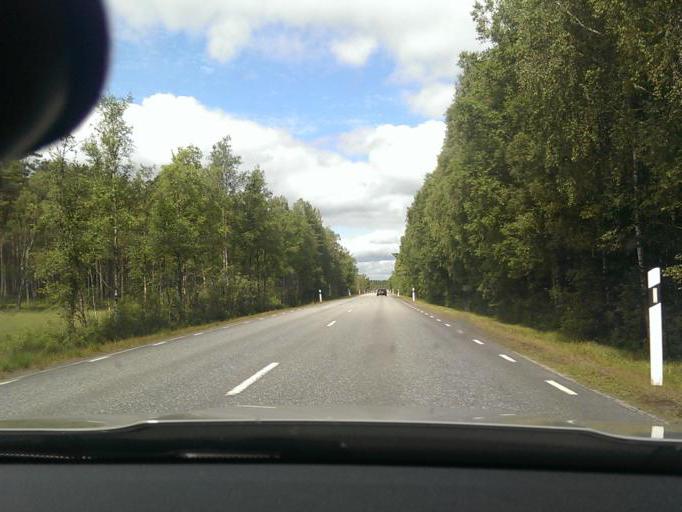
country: SE
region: Joenkoeping
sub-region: Gnosjo Kommun
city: Hillerstorp
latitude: 57.2881
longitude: 13.9518
